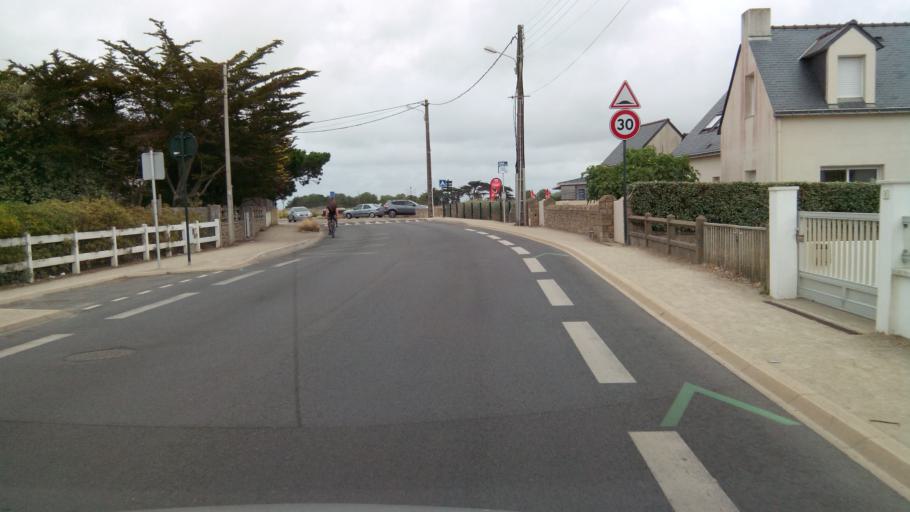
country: FR
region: Pays de la Loire
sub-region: Departement de la Loire-Atlantique
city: Batz-sur-Mer
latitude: 47.2777
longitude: -2.4925
